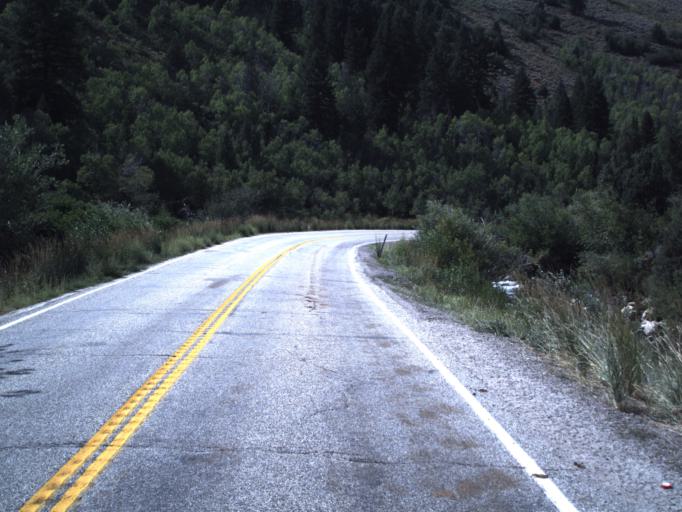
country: US
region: Utah
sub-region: Cache County
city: North Logan
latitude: 41.8517
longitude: -111.5852
